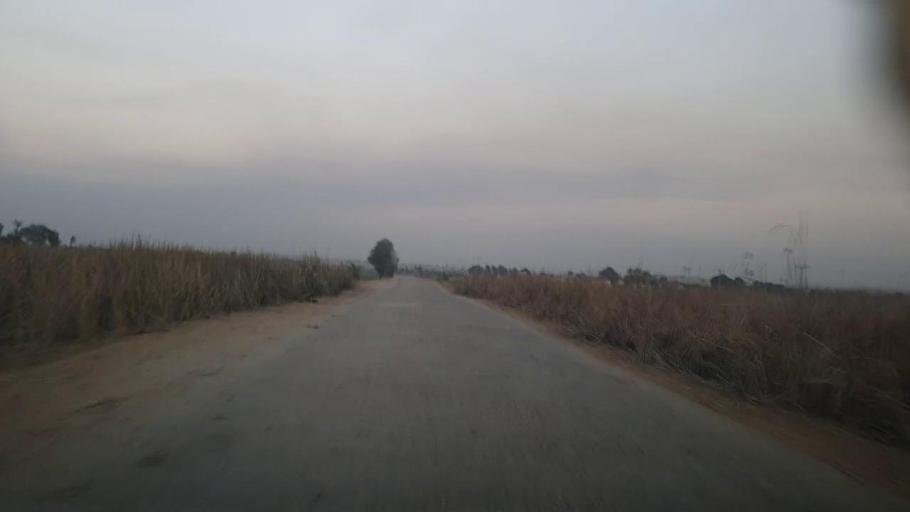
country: PK
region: Sindh
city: Kandiari
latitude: 26.6769
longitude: 68.9478
